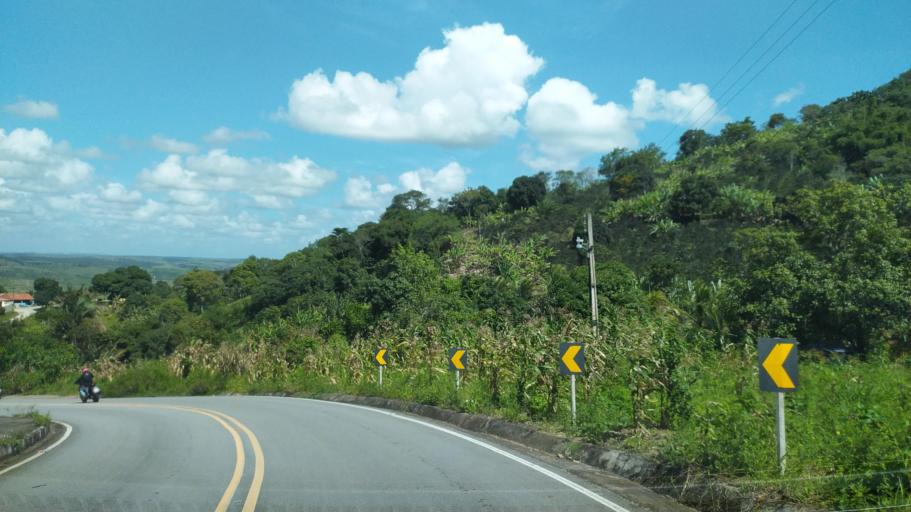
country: BR
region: Alagoas
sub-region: Uniao Dos Palmares
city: Uniao dos Palmares
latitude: -9.1639
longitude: -36.0681
